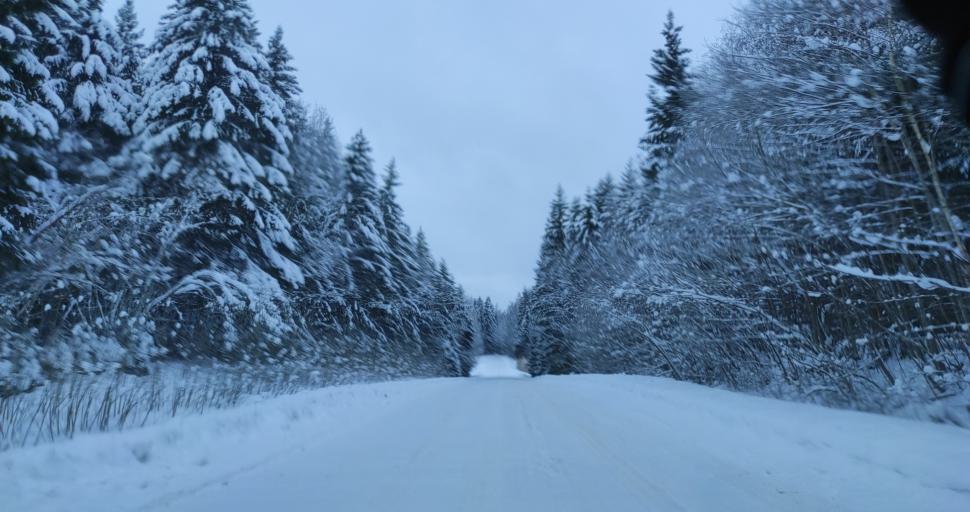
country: LV
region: Vecpiebalga
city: Vecpiebalga
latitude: 56.8761
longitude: 25.9675
